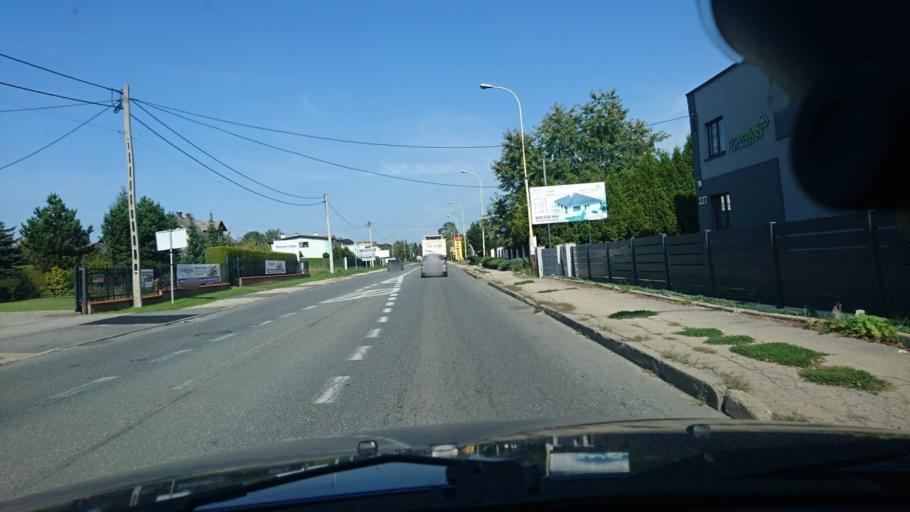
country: PL
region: Silesian Voivodeship
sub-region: Powiat bielski
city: Bestwina
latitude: 49.8845
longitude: 19.0255
